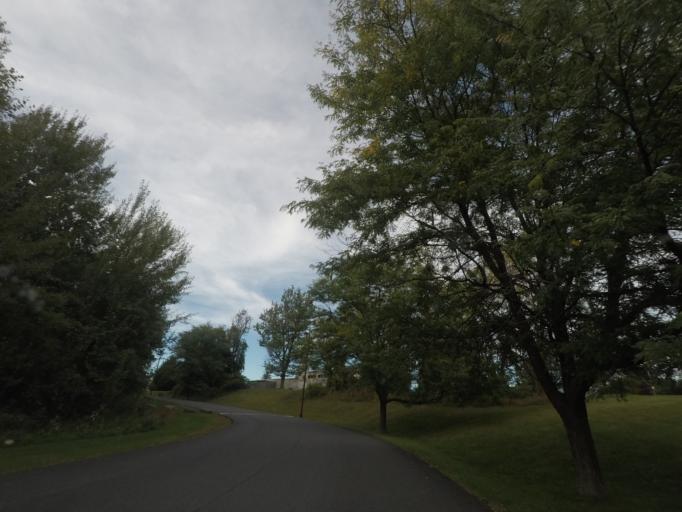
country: US
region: New York
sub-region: Rensselaer County
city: East Greenbush
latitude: 42.5955
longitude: -73.7081
